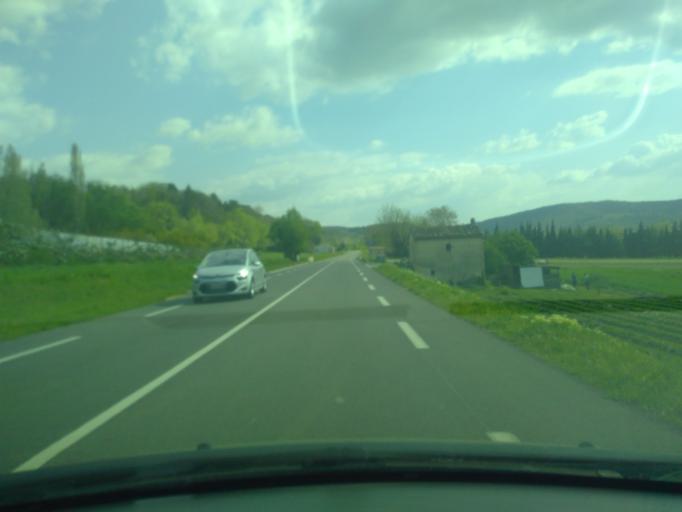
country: FR
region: Provence-Alpes-Cote d'Azur
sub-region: Departement du Vaucluse
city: Malaucene
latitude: 44.1924
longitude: 5.1195
